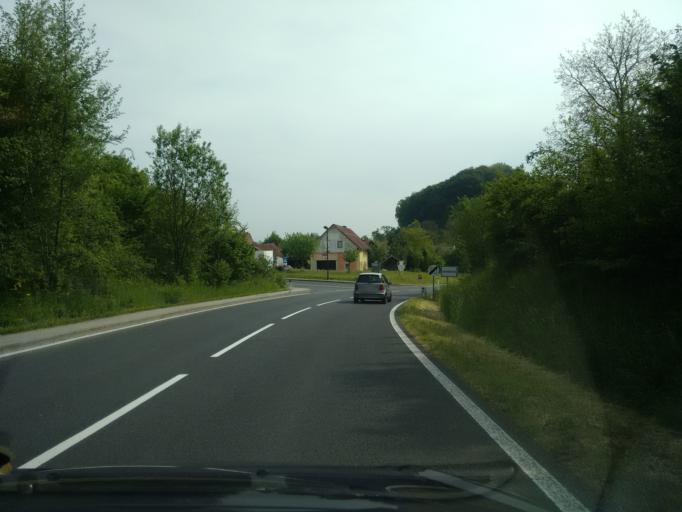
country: AT
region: Upper Austria
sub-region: Wels Stadt
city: Wels
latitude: 48.1585
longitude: 14.0743
